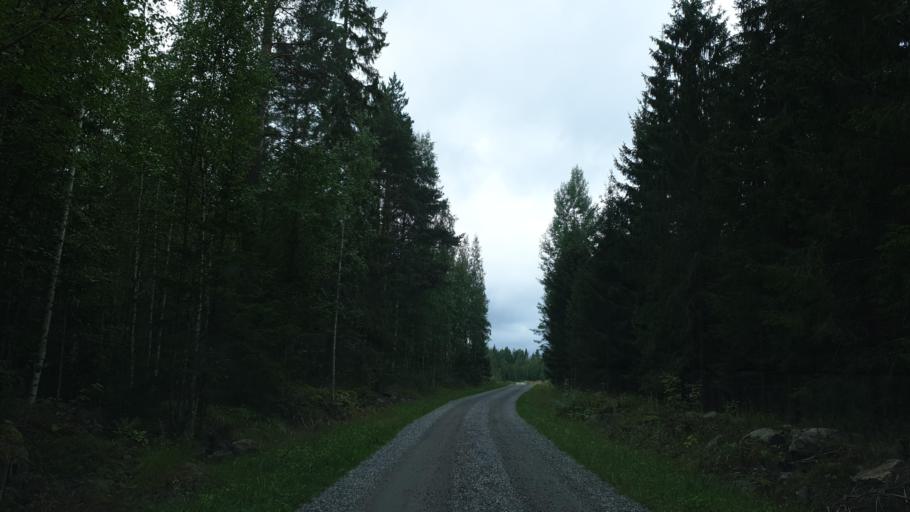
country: FI
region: Northern Savo
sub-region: Kuopio
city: Nilsiae
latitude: 63.2471
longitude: 28.2577
